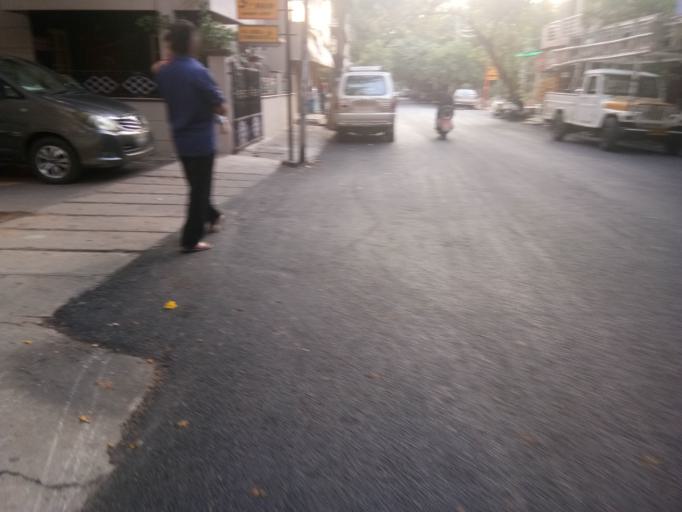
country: IN
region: Karnataka
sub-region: Bangalore Urban
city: Bangalore
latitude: 13.0183
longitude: 77.6349
